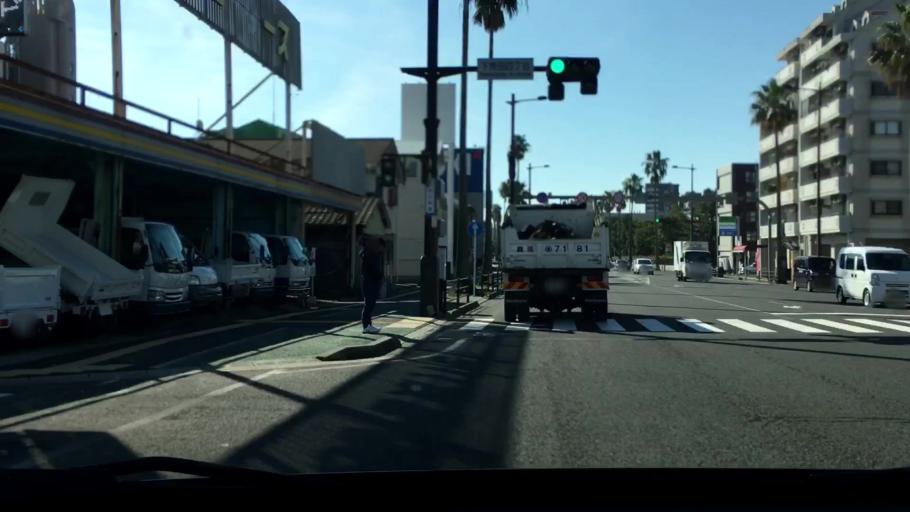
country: JP
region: Kagoshima
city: Kagoshima-shi
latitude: 31.5702
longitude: 130.5591
